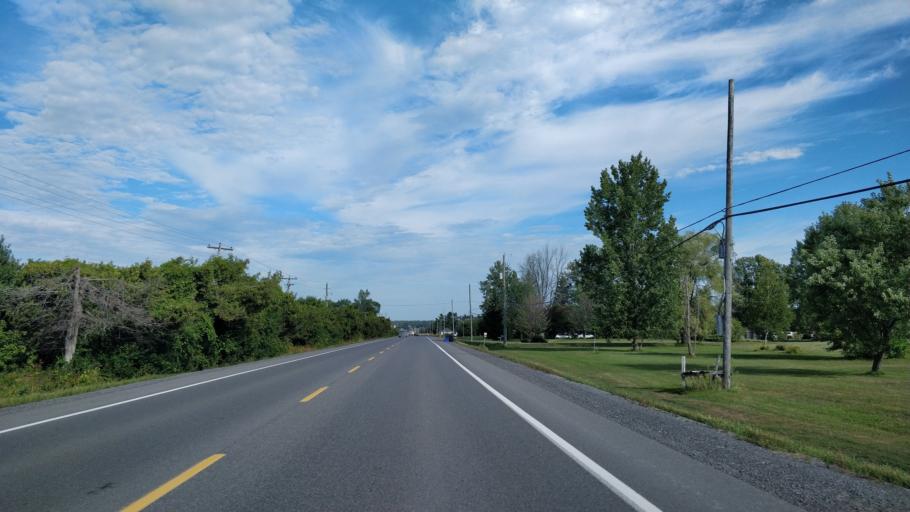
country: CA
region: Ontario
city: Bells Corners
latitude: 45.3263
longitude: -76.0130
